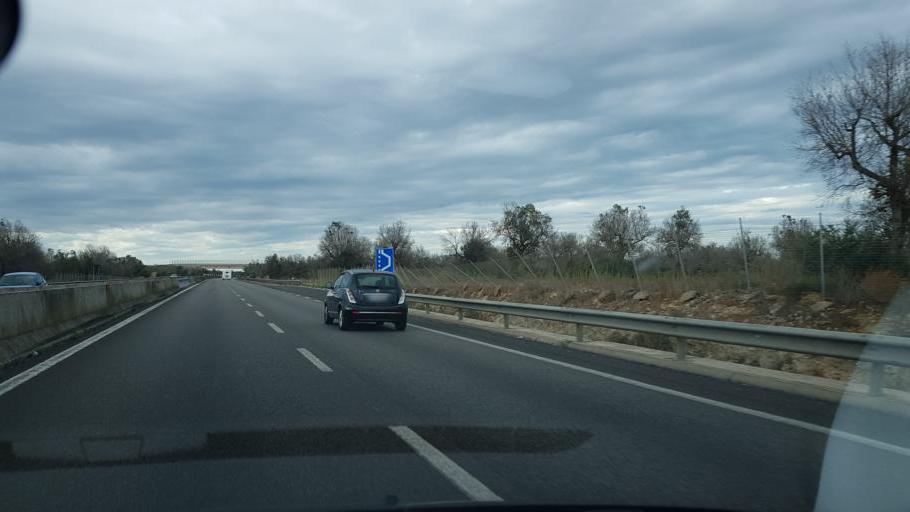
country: IT
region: Apulia
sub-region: Provincia di Lecce
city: Trepuzzi
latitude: 40.4217
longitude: 18.0943
